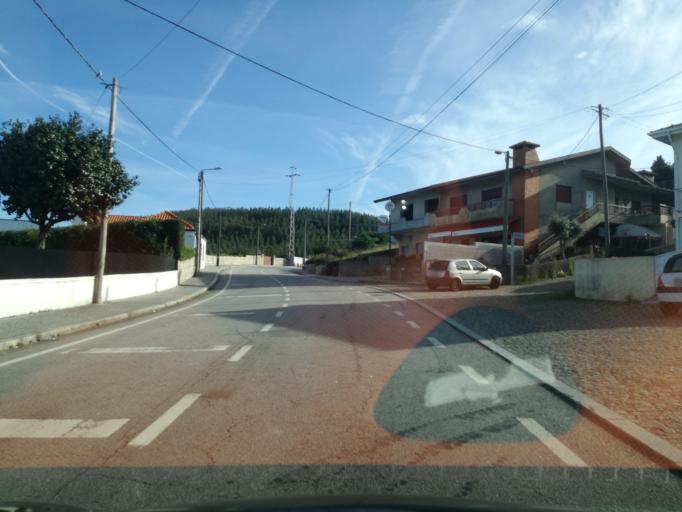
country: PT
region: Porto
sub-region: Trofa
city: Sao Romao do Coronado
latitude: 41.2783
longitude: -8.5248
